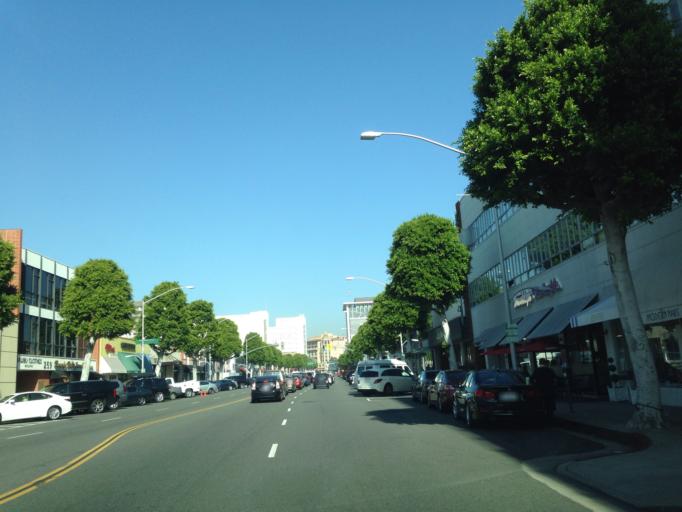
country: US
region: California
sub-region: Los Angeles County
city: Beverly Hills
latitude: 34.0624
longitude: -118.3990
